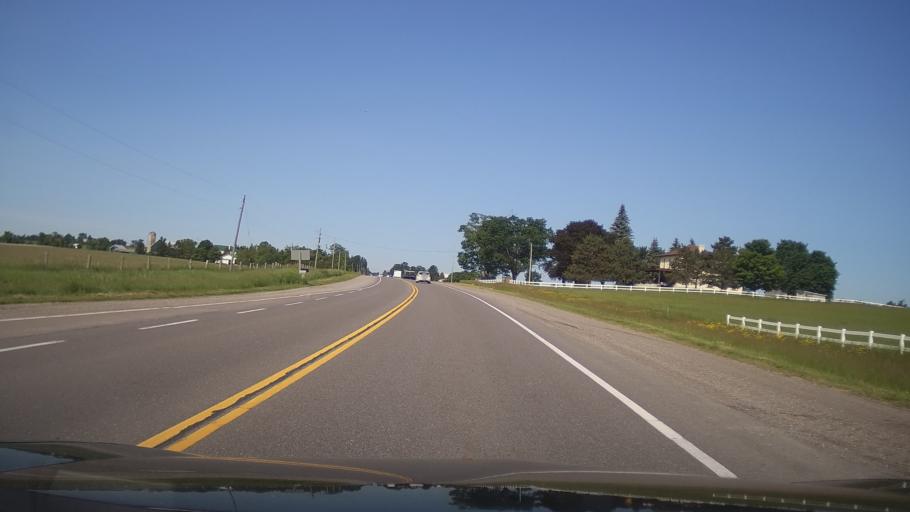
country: CA
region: Ontario
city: Omemee
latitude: 44.3462
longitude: -78.8208
